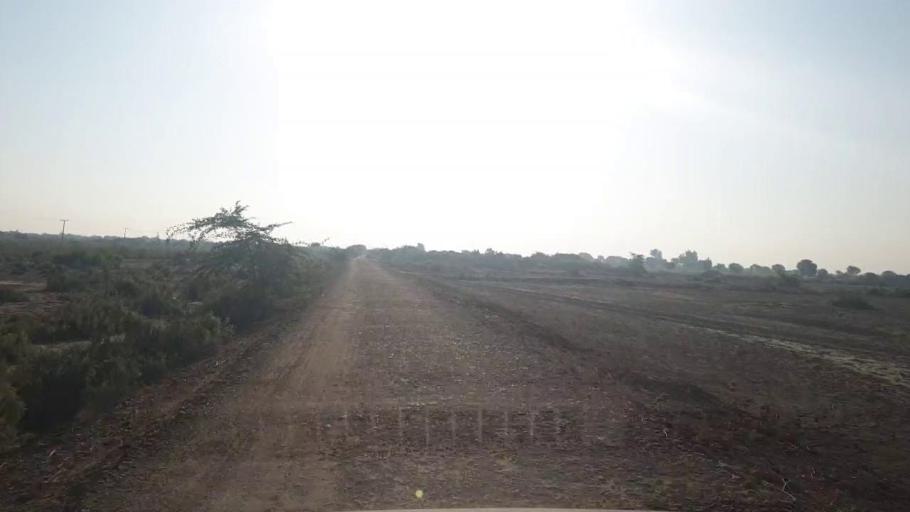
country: PK
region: Sindh
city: Badin
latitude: 24.7357
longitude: 68.8718
